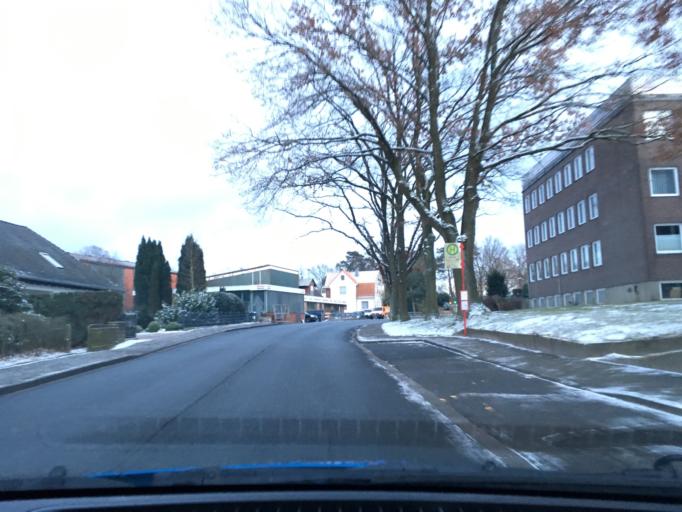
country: DE
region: Lower Saxony
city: Lueneburg
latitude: 53.2224
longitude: 10.3848
